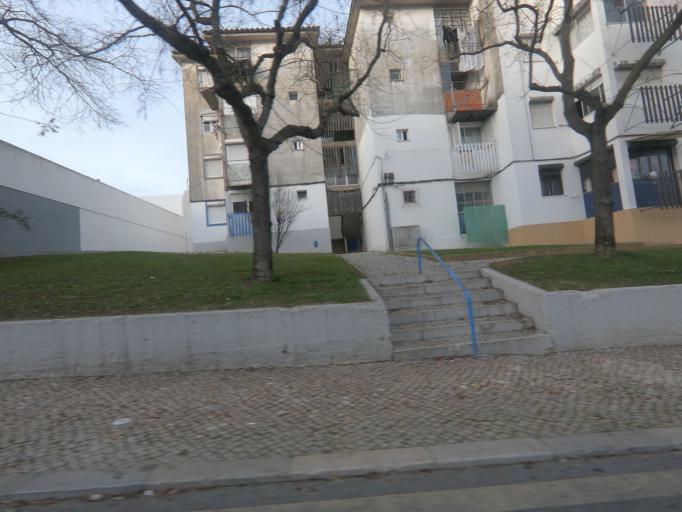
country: PT
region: Setubal
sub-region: Setubal
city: Setubal
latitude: 38.5303
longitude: -8.8709
